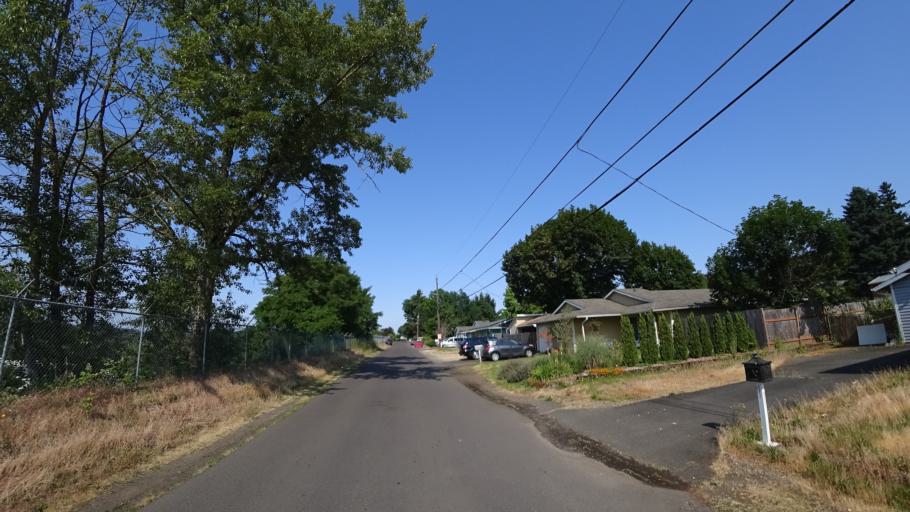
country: US
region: Oregon
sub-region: Multnomah County
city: Lents
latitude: 45.4586
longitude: -122.5960
